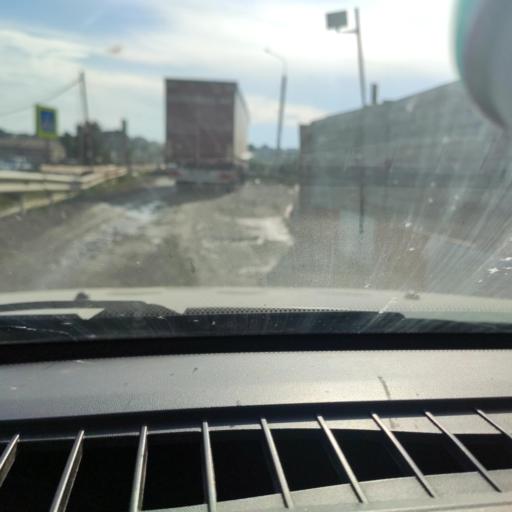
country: RU
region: Kirov
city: Kostino
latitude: 58.8526
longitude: 53.2247
